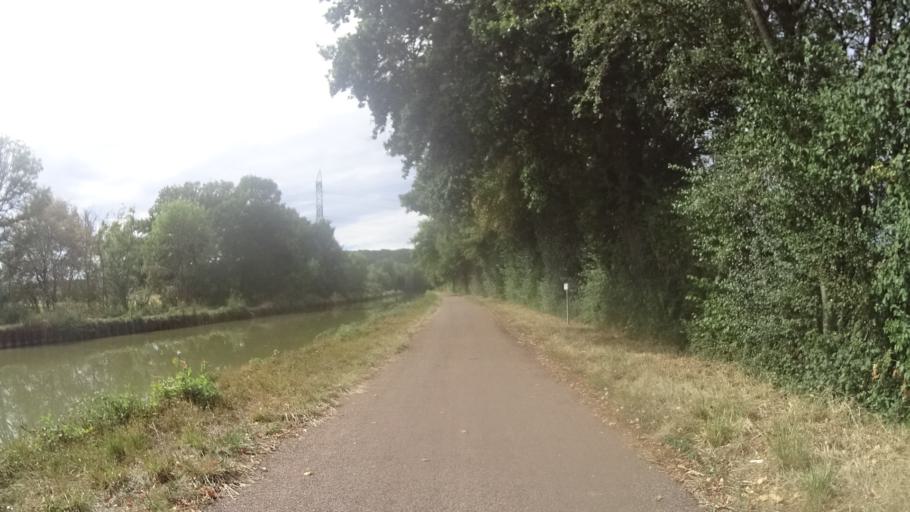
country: FR
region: Bourgogne
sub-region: Departement de la Nievre
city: Sermoise-sur-Loire
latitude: 46.9356
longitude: 3.2112
